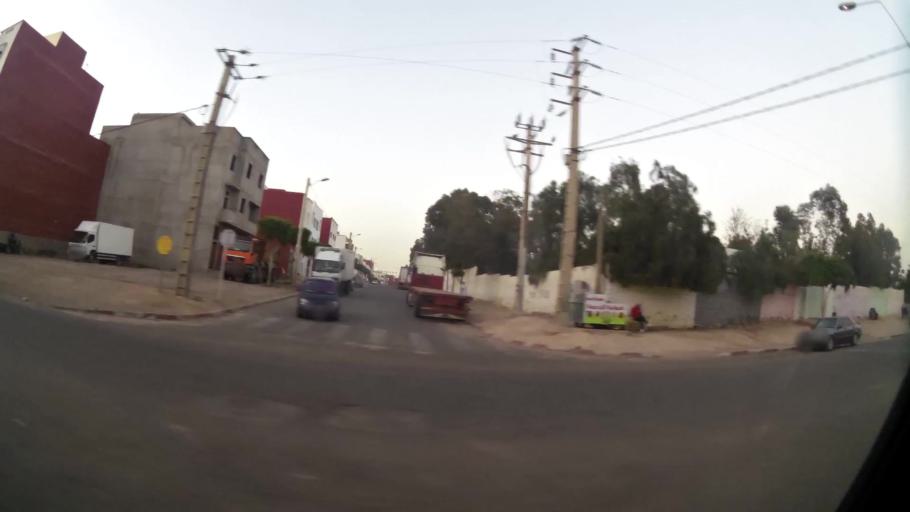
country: MA
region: Souss-Massa-Draa
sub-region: Inezgane-Ait Mellou
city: Inezgane
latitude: 30.3774
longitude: -9.4977
